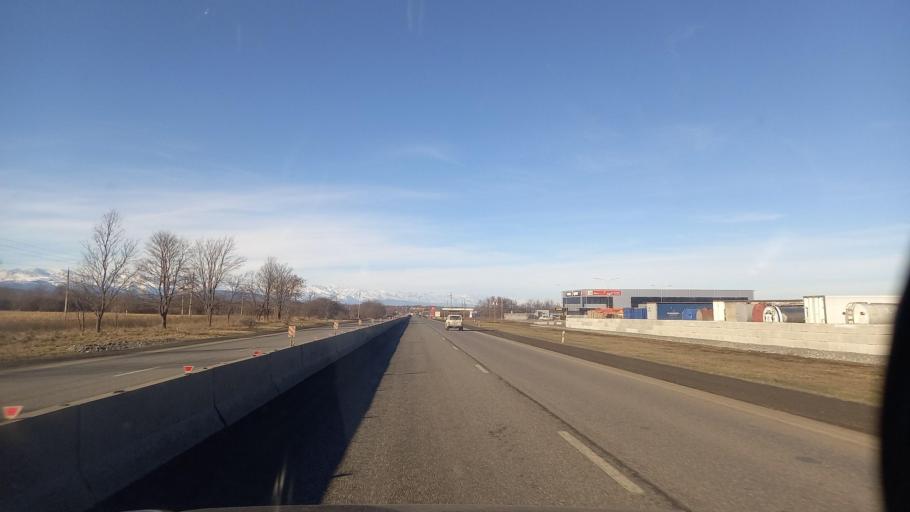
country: RU
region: North Ossetia
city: Gizel'
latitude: 43.0264
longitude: 44.6182
